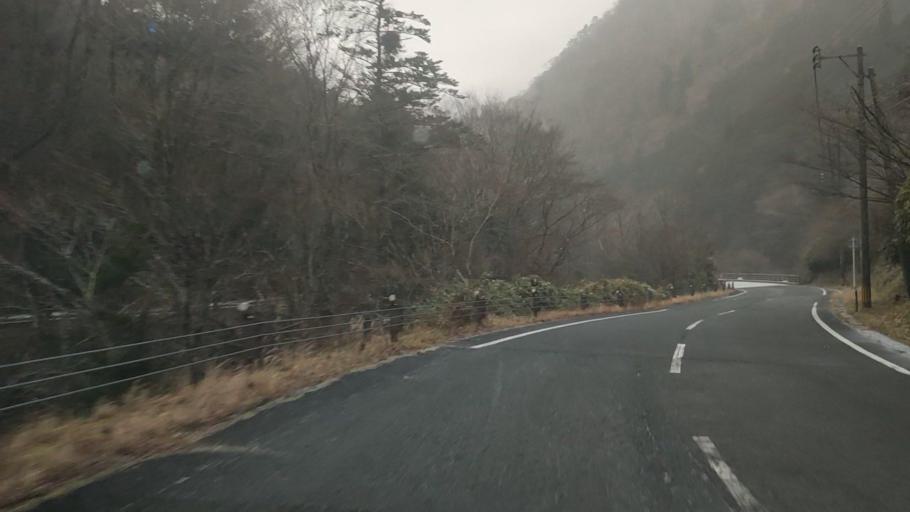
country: JP
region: Kumamoto
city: Matsubase
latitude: 32.5647
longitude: 130.9134
